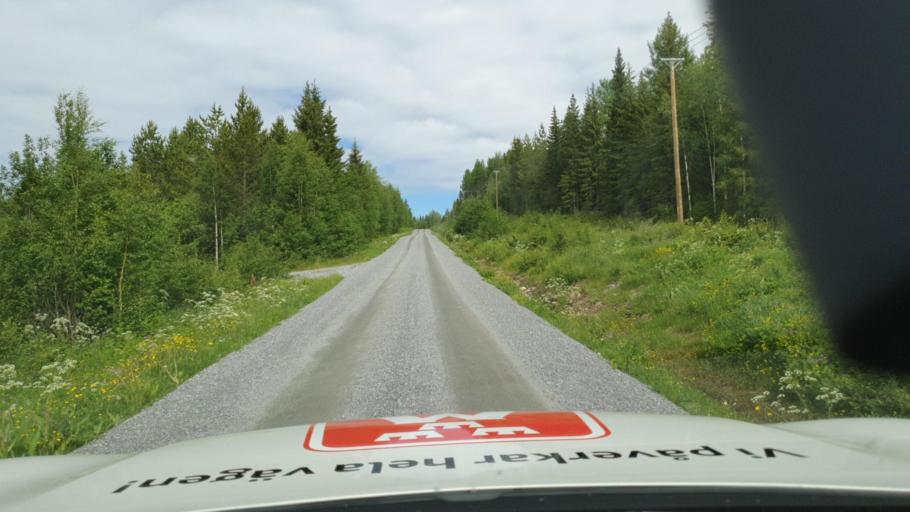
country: SE
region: Vaesterbotten
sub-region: Skelleftea Kommun
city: Langsele
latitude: 64.6132
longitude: 20.2710
